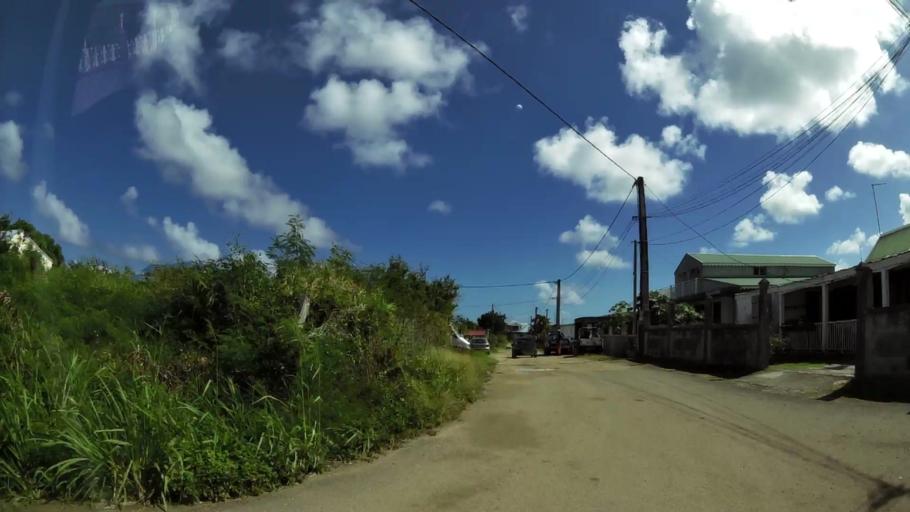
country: GP
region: Guadeloupe
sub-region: Guadeloupe
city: Anse-Bertrand
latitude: 16.4674
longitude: -61.4993
